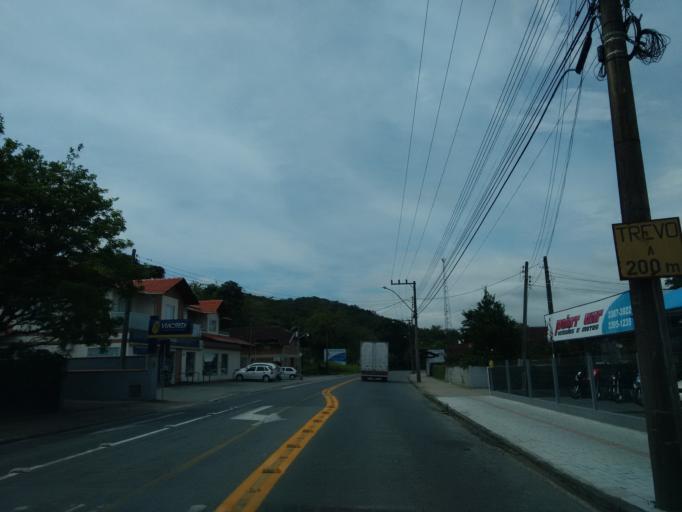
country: BR
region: Santa Catarina
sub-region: Pomerode
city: Pomerode
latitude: -26.7108
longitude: -49.1642
